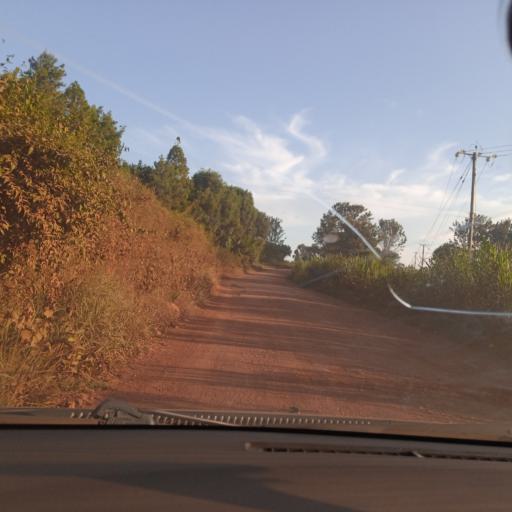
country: UG
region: Central Region
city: Masaka
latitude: -0.3396
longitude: 31.7625
